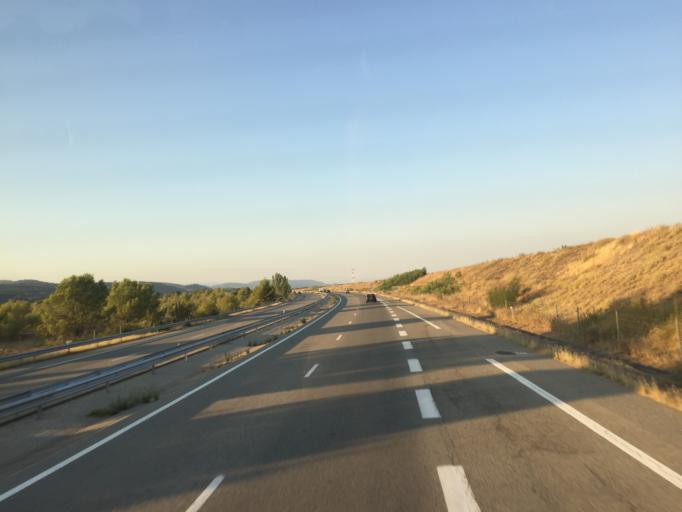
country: FR
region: Provence-Alpes-Cote d'Azur
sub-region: Departement du Vaucluse
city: Beaumont-de-Pertuis
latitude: 43.7082
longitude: 5.7338
